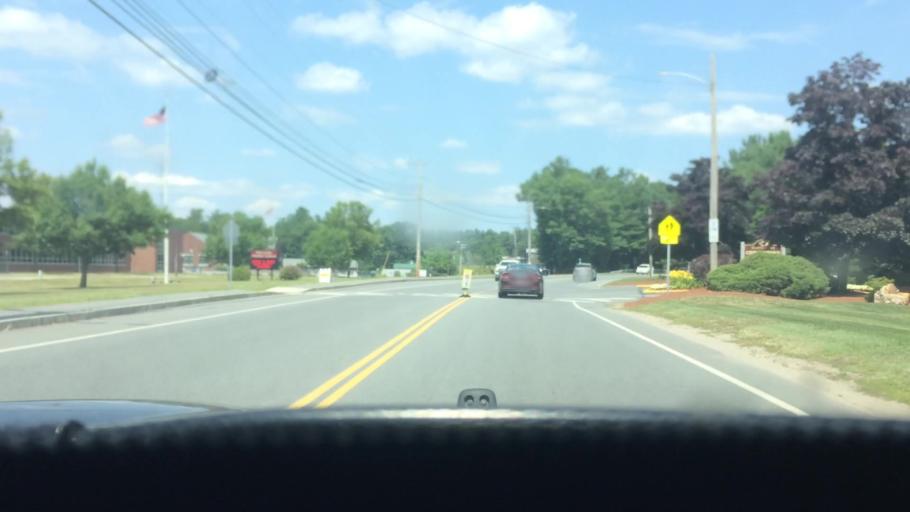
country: US
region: Massachusetts
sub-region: Middlesex County
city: Chelmsford
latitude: 42.6188
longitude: -71.3655
